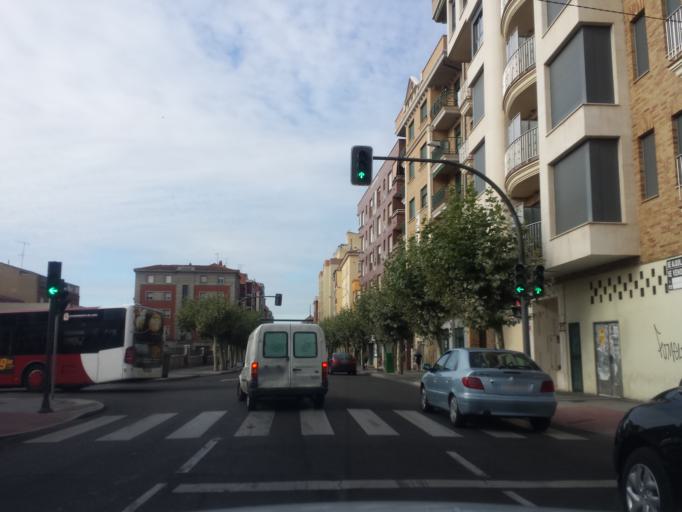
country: ES
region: Castille and Leon
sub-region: Provincia de Leon
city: Leon
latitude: 42.6100
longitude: -5.5719
